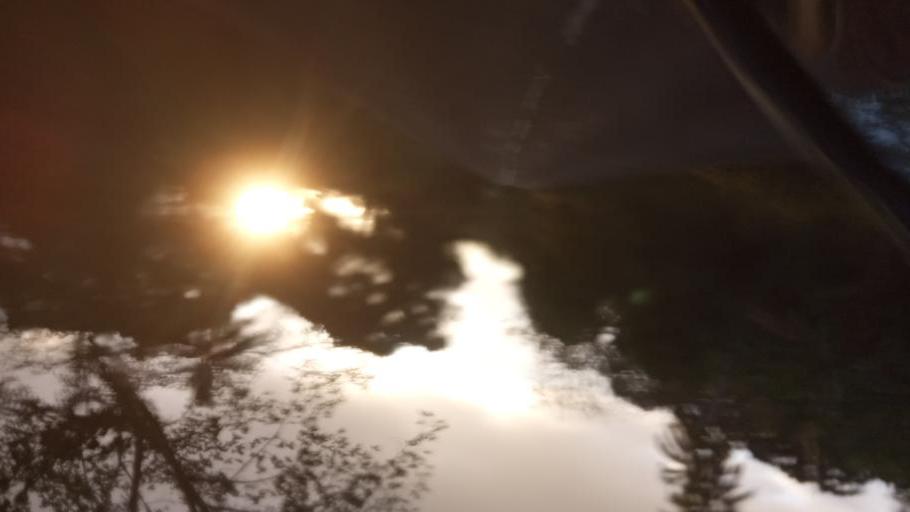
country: YT
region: Kani-Keli
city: Kani Keli
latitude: -12.9257
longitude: 45.1095
